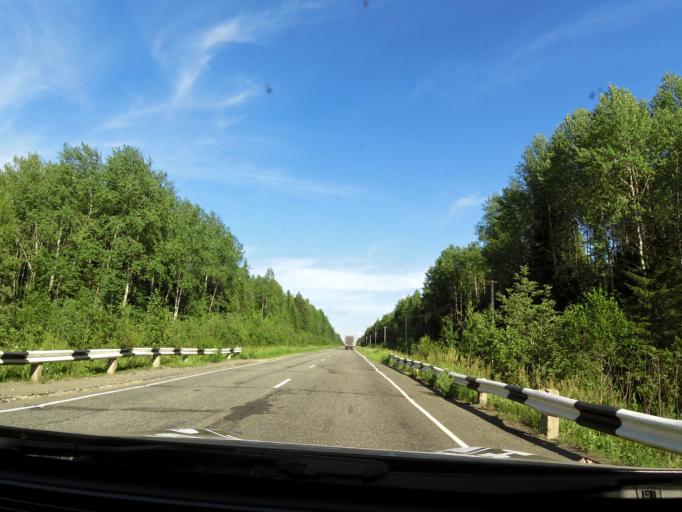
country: RU
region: Kirov
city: Belaya Kholunitsa
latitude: 58.9187
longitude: 51.1315
